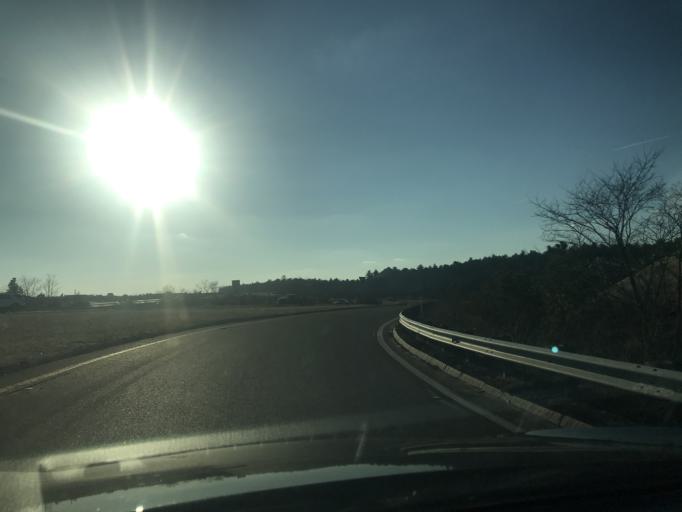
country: US
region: Massachusetts
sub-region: Plymouth County
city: North Plymouth
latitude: 41.9615
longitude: -70.7095
